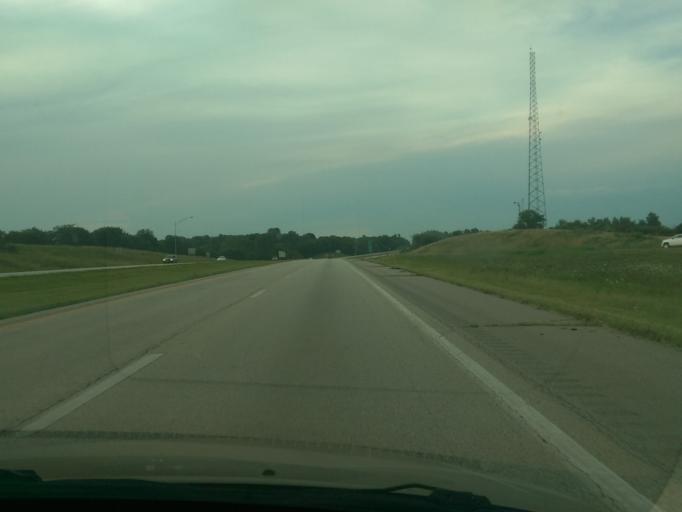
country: US
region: Missouri
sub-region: Andrew County
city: Country Club Village
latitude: 39.8164
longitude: -94.8040
